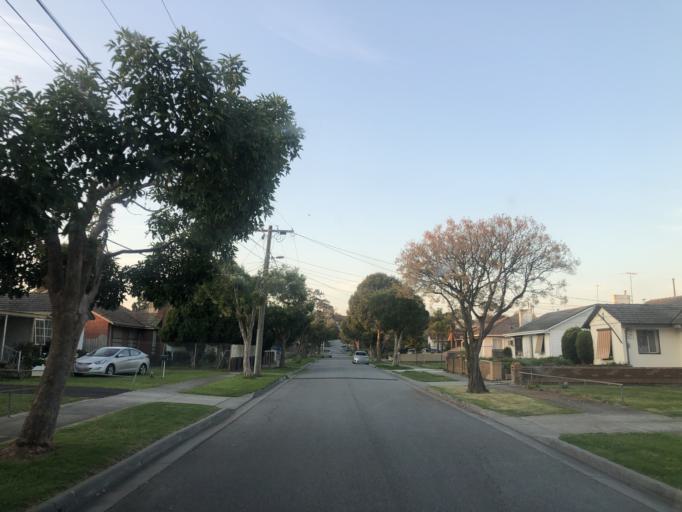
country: AU
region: Victoria
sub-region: Casey
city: Doveton
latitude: -37.9967
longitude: 145.2356
